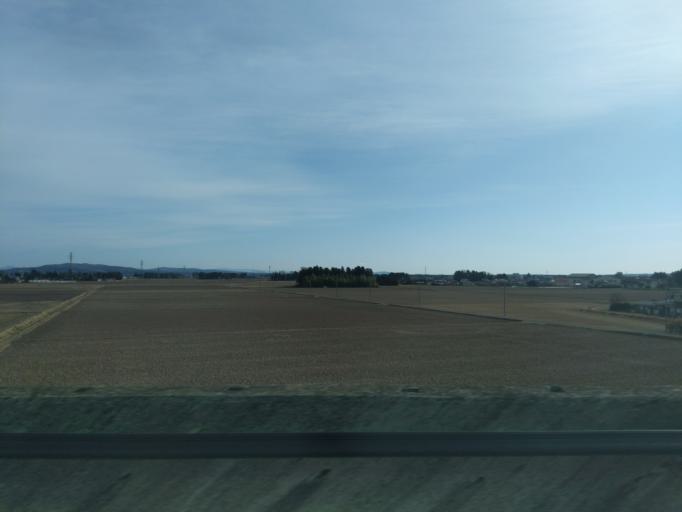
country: JP
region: Miyagi
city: Furukawa
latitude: 38.5994
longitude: 140.9820
